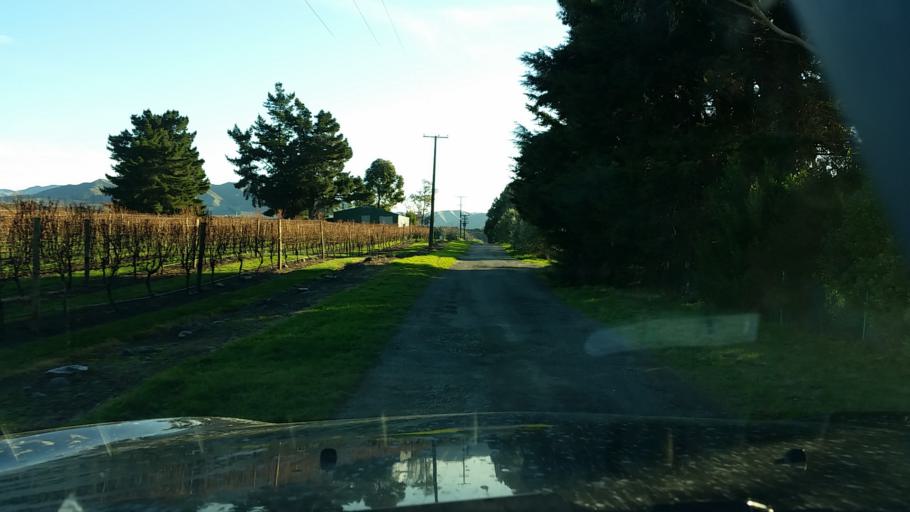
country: NZ
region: Marlborough
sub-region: Marlborough District
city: Blenheim
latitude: -41.6674
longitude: 174.0663
